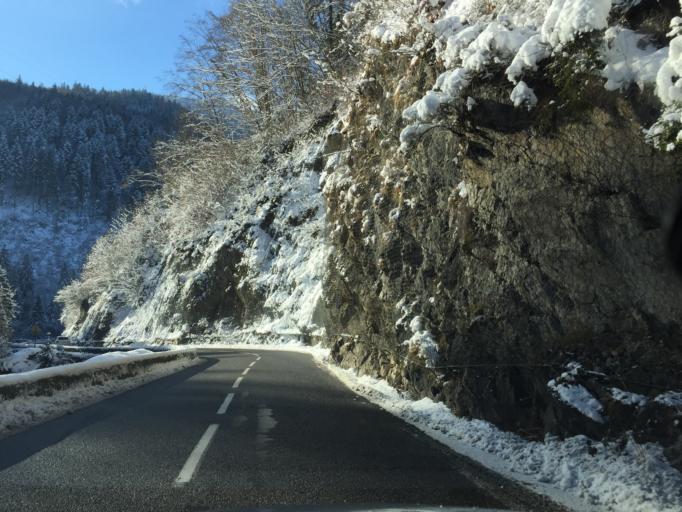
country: FR
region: Rhone-Alpes
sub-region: Departement de la Haute-Savoie
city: Feternes
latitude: 46.3271
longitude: 6.5971
